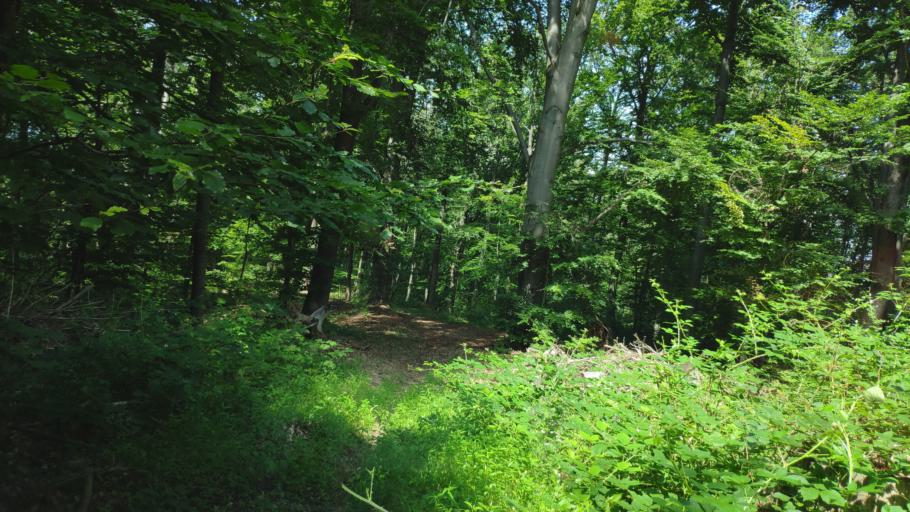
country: SK
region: Kosicky
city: Dobsina
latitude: 48.7067
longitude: 20.3834
